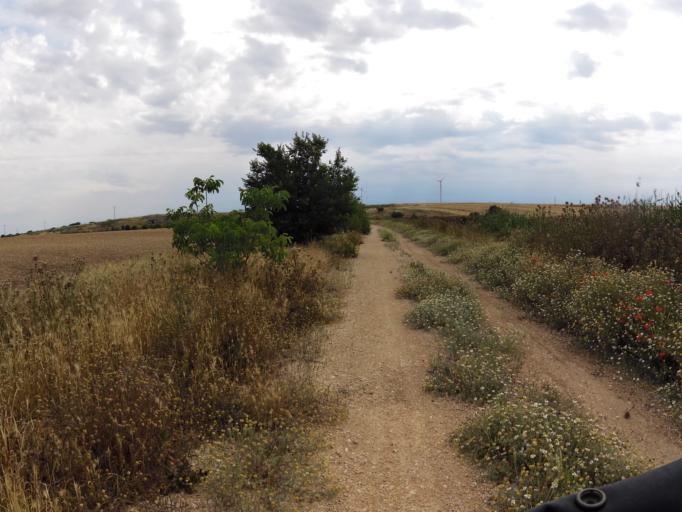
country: ES
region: Castille-La Mancha
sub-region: Provincia de Albacete
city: Albacete
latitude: 39.0414
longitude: -1.7655
